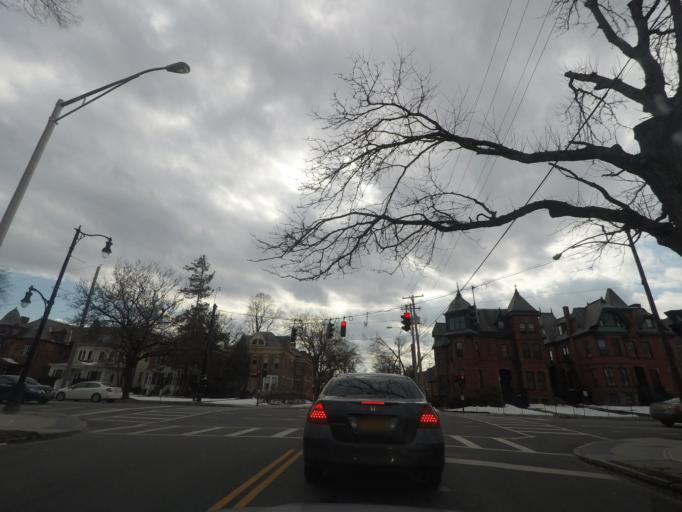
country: US
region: New York
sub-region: Albany County
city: Albany
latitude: 42.6582
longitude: -73.7773
